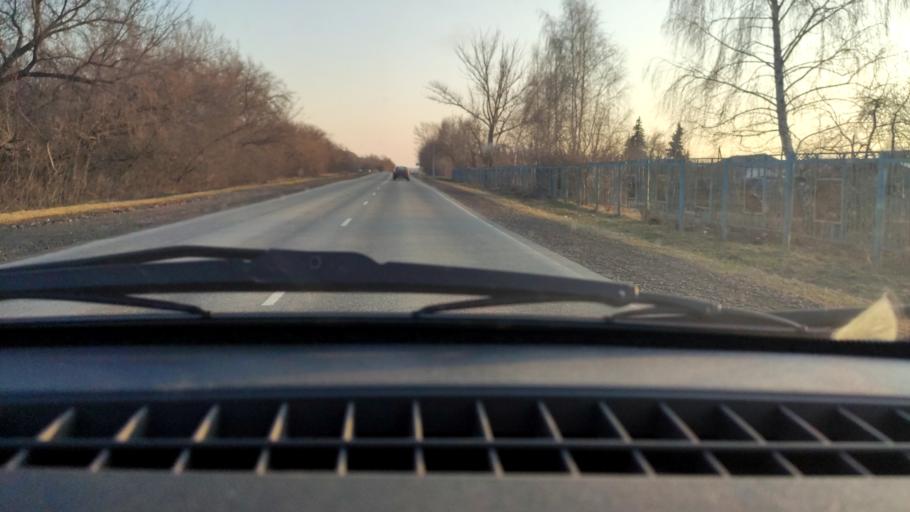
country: RU
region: Bashkortostan
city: Davlekanovo
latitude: 54.2970
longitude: 55.1279
